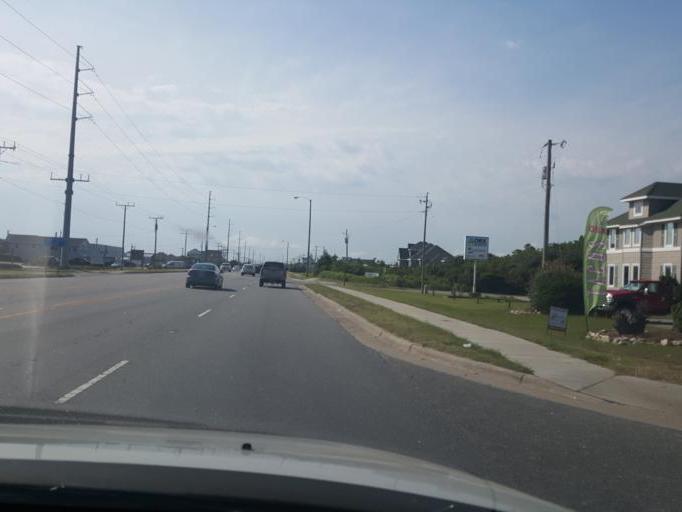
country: US
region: North Carolina
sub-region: Dare County
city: Kill Devil Hills
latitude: 36.0460
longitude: -75.6806
